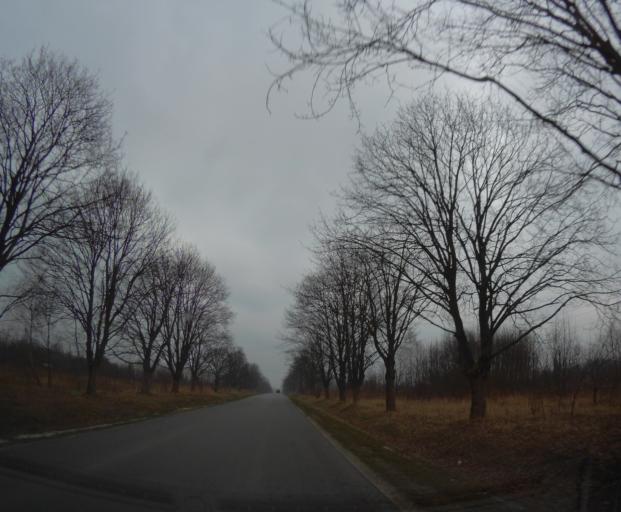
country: PL
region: Lublin Voivodeship
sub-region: Powiat bilgorajski
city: Bilgoraj
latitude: 50.5406
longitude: 22.6917
